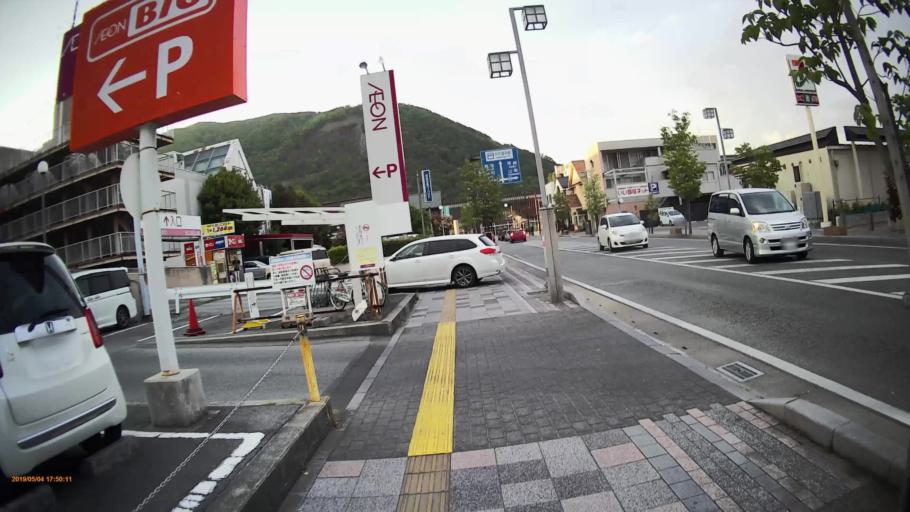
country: JP
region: Yamanashi
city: Isawa
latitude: 35.6560
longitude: 138.6353
